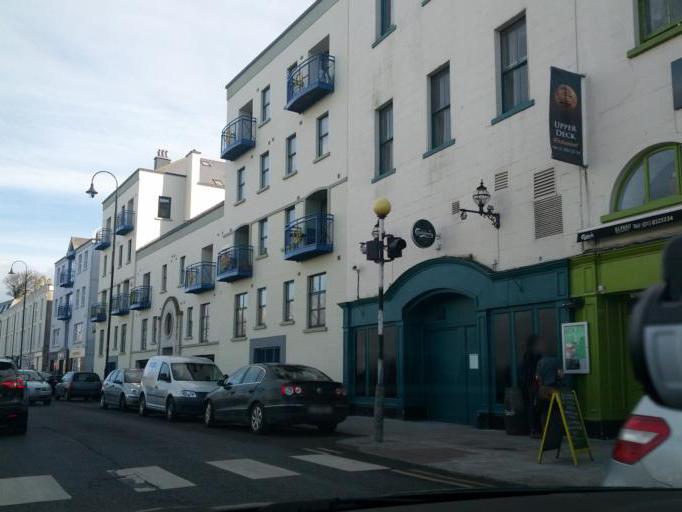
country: IE
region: Leinster
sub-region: Fingal County
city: Howth
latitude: 53.3879
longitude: -6.0688
